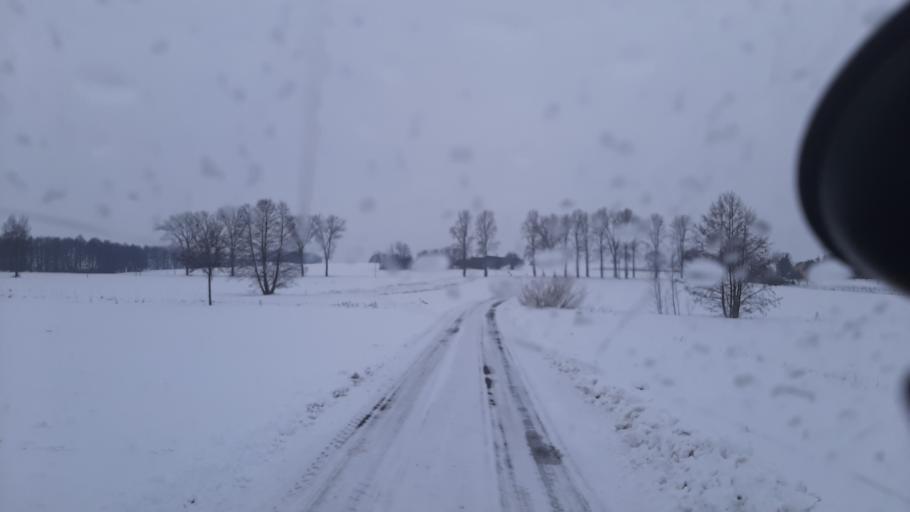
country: PL
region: Lublin Voivodeship
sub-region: Powiat lubelski
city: Jastkow
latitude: 51.3480
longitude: 22.3921
